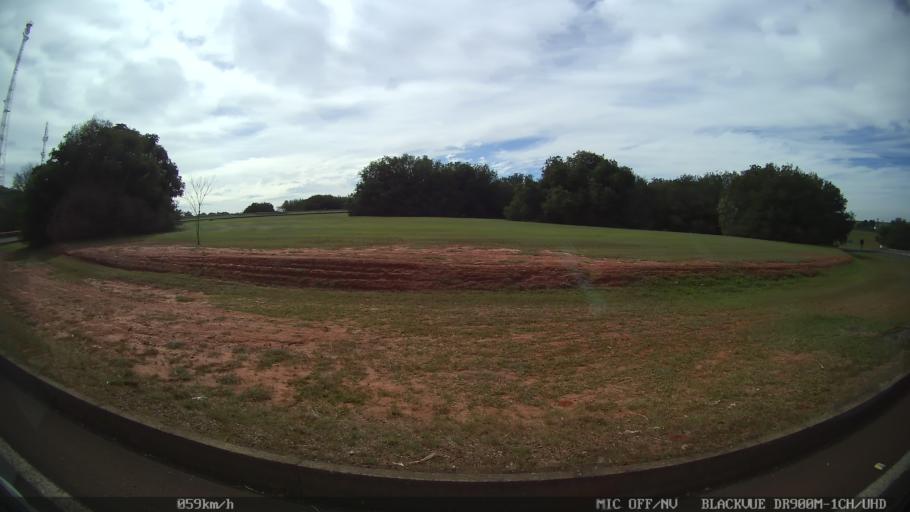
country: BR
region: Sao Paulo
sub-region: Taquaritinga
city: Taquaritinga
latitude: -21.4755
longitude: -48.6009
